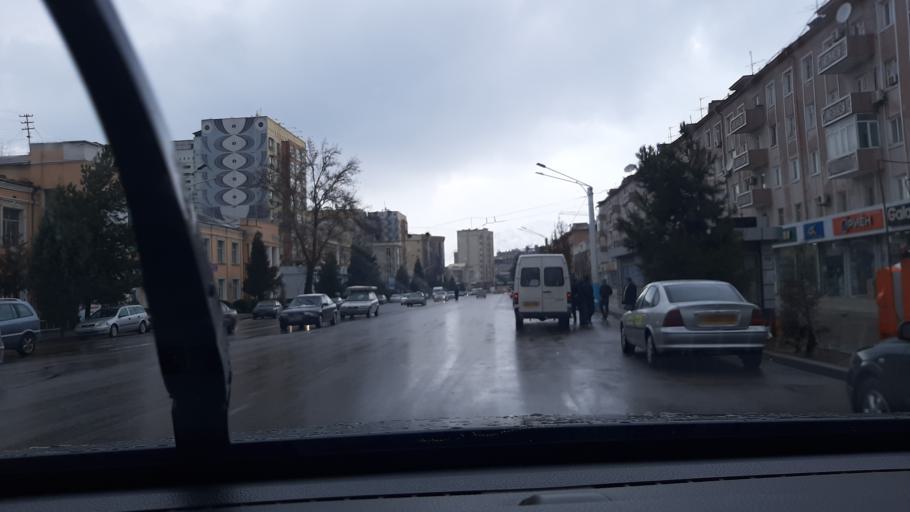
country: TJ
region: Viloyati Sughd
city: Khujand
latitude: 40.2784
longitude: 69.6294
